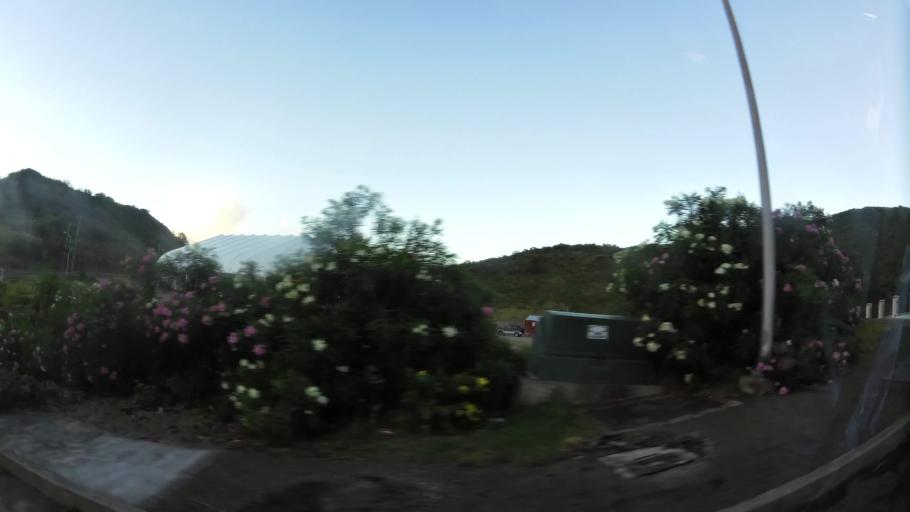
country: MS
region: Saint Peter
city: Brades
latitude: 16.7977
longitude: -62.2027
